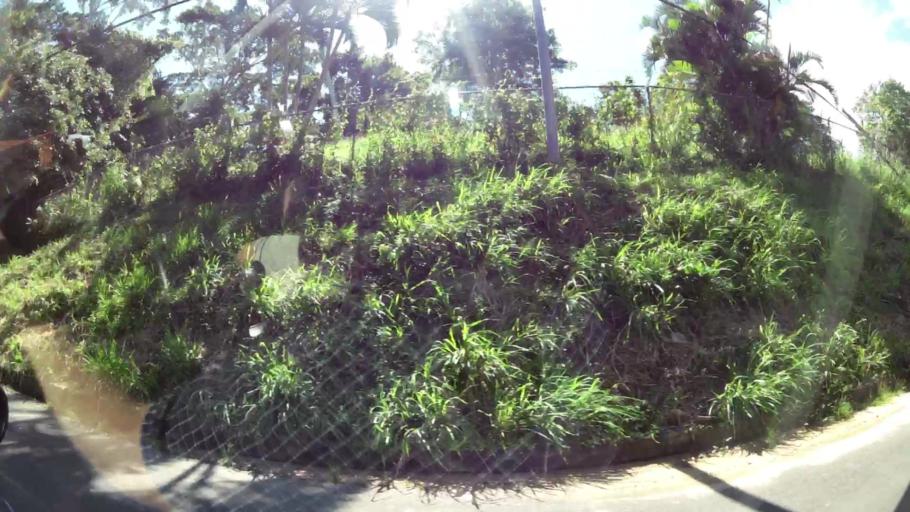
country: TT
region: Tobago
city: Scarborough
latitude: 11.2214
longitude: -60.7697
